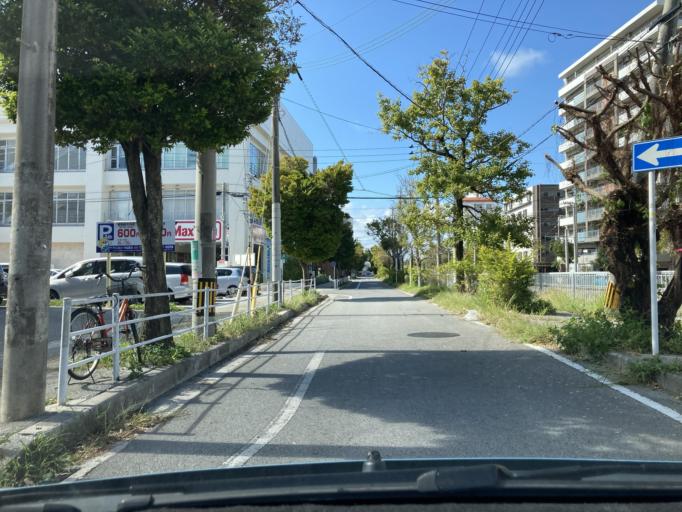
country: JP
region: Okinawa
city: Naha-shi
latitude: 26.2212
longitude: 127.6816
